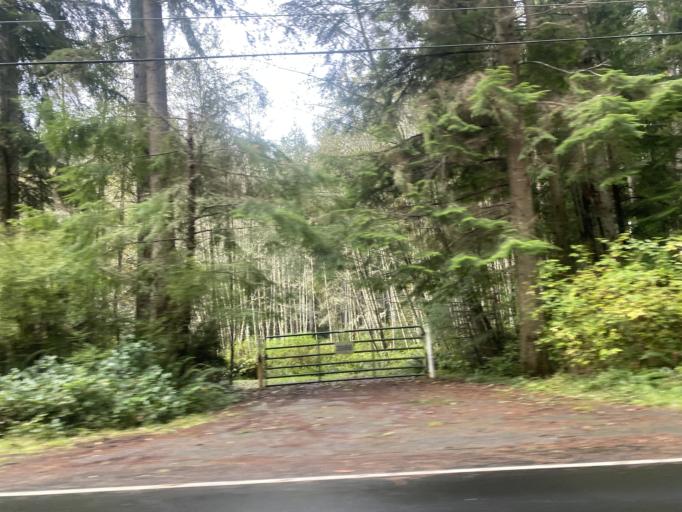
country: US
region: Washington
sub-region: Island County
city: Freeland
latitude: 48.0667
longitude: -122.4850
